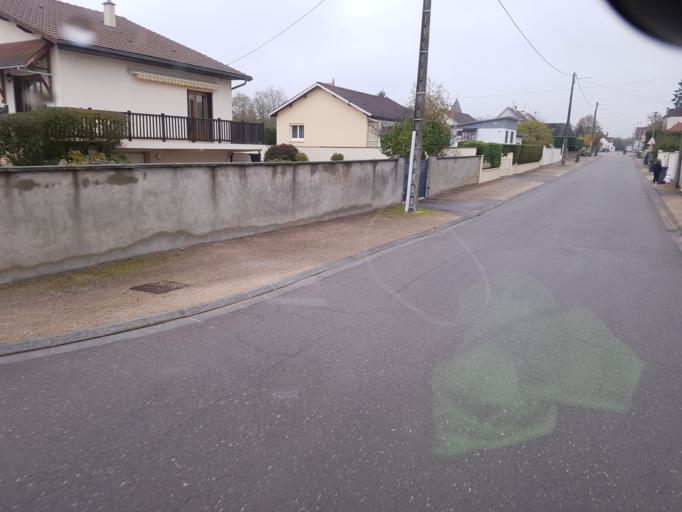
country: FR
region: Bourgogne
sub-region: Departement de la Cote-d'Or
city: Genlis
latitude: 47.2785
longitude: 5.2193
